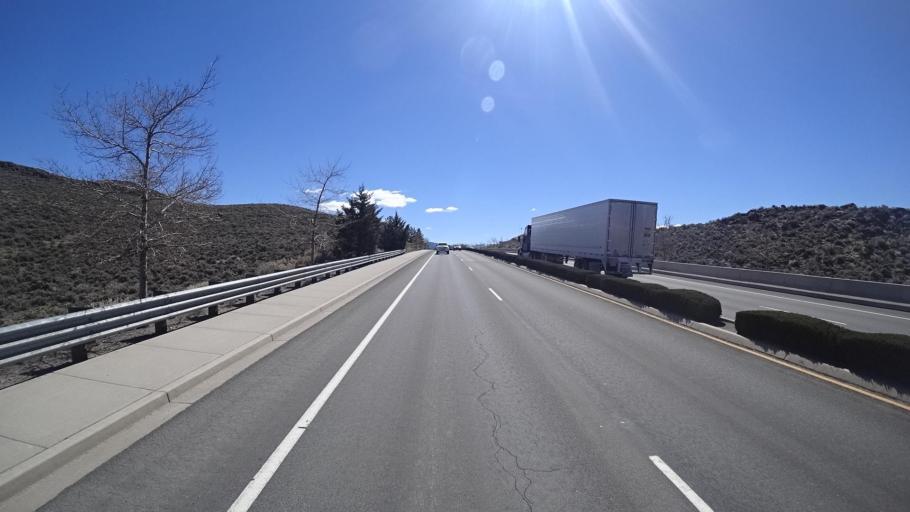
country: US
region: Nevada
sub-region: Washoe County
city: Sparks
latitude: 39.4604
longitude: -119.7633
